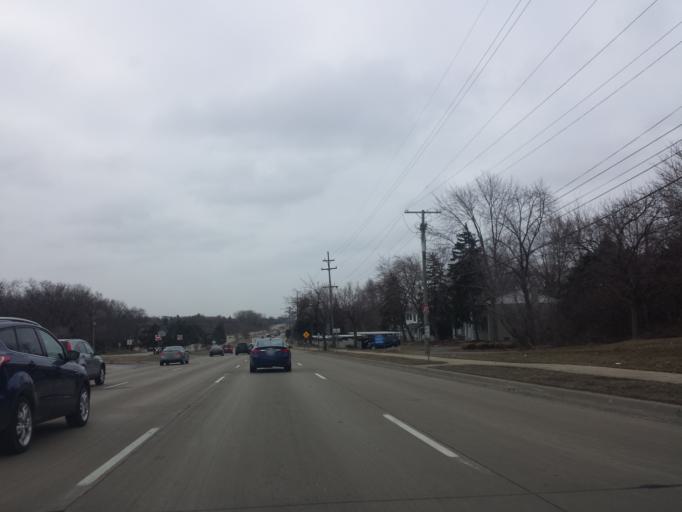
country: US
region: Michigan
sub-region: Oakland County
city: Bingham Farms
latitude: 42.5392
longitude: -83.2851
